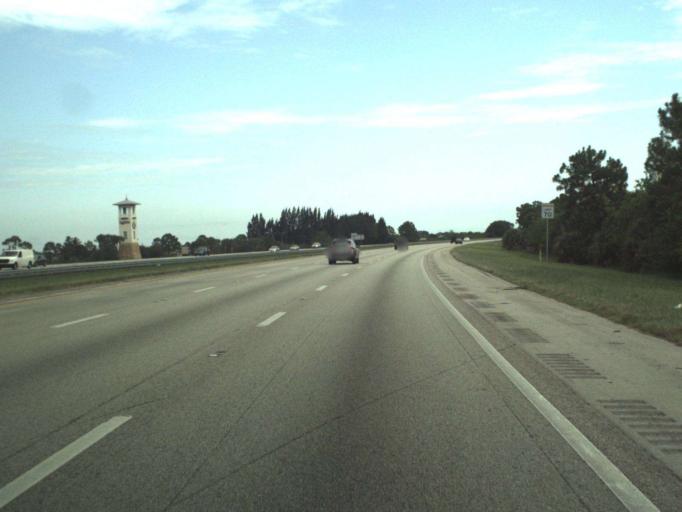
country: US
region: Florida
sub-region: Saint Lucie County
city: Port Saint Lucie
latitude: 27.2748
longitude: -80.4256
